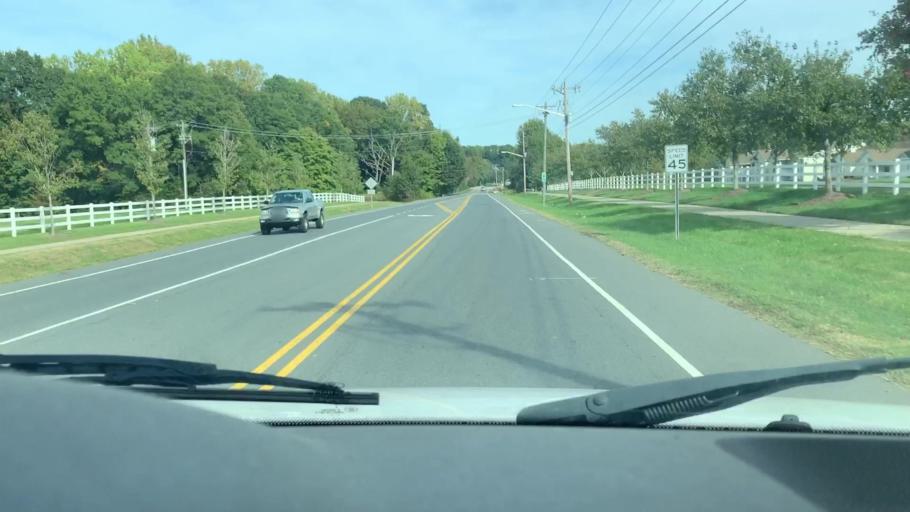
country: US
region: North Carolina
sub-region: Mecklenburg County
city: Cornelius
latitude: 35.4627
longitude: -80.8801
